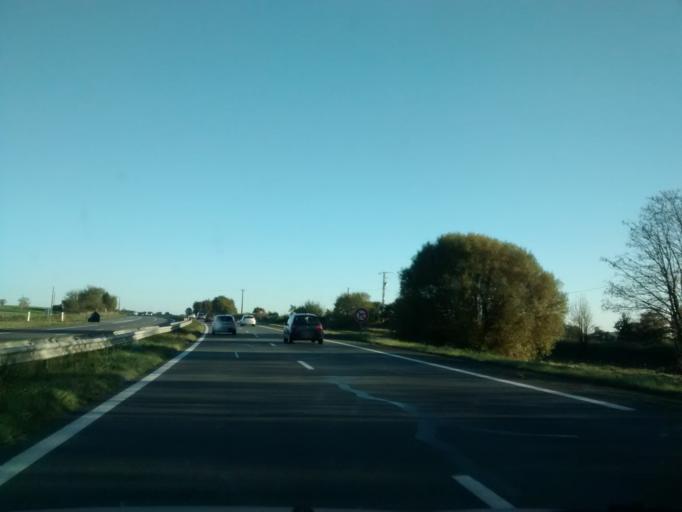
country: FR
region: Brittany
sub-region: Departement d'Ille-et-Vilaine
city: Quedillac
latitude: 48.2213
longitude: -2.1104
